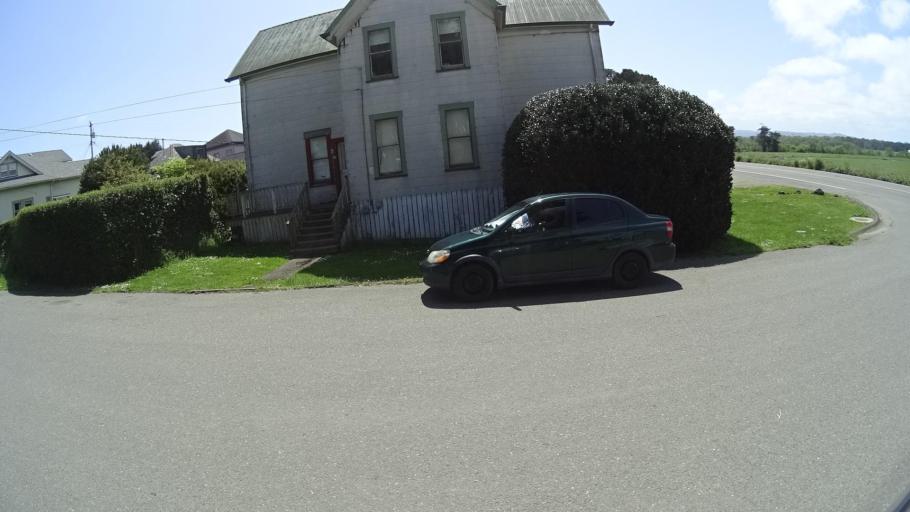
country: US
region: California
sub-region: Humboldt County
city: Ferndale
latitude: 40.6406
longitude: -124.2257
